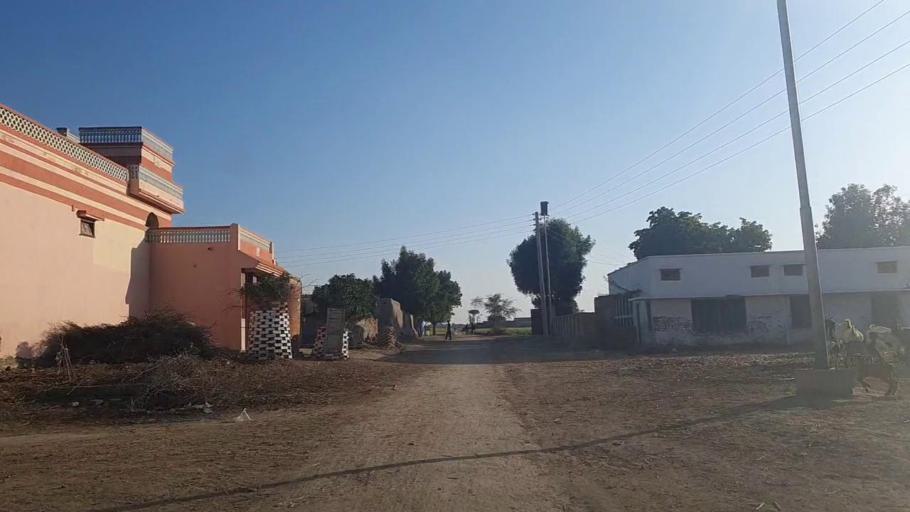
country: PK
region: Sindh
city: Jam Sahib
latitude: 26.2942
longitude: 68.6616
